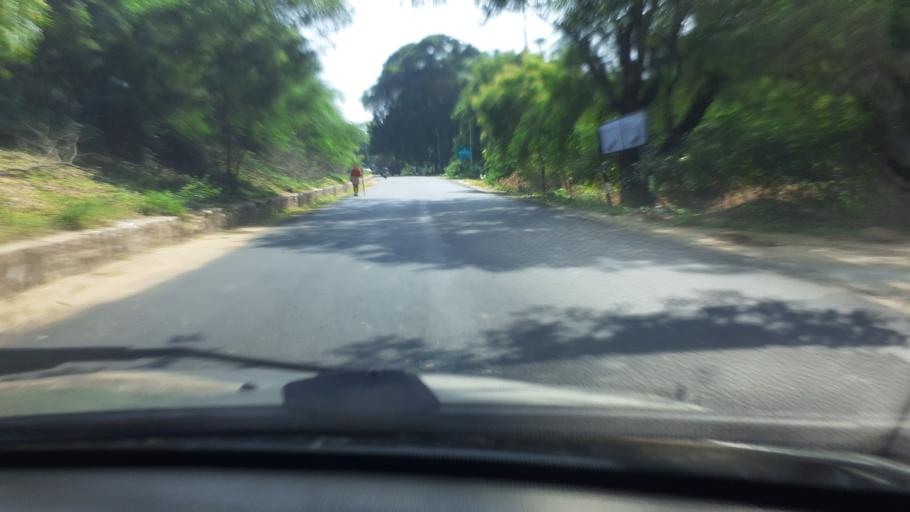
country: IN
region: Tamil Nadu
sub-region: Thoothukkudi
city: Alwar Tirunagari
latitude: 8.6095
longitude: 77.9275
